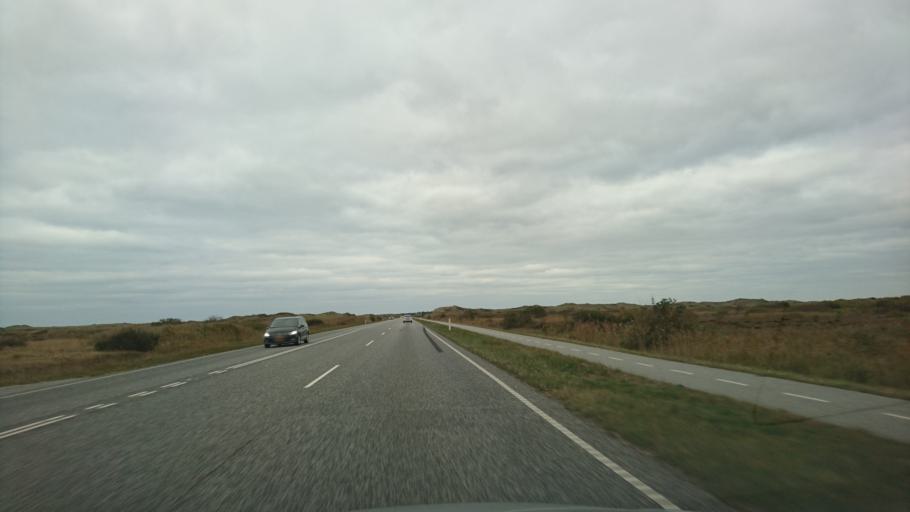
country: DK
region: North Denmark
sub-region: Frederikshavn Kommune
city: Skagen
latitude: 57.6798
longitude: 10.4619
